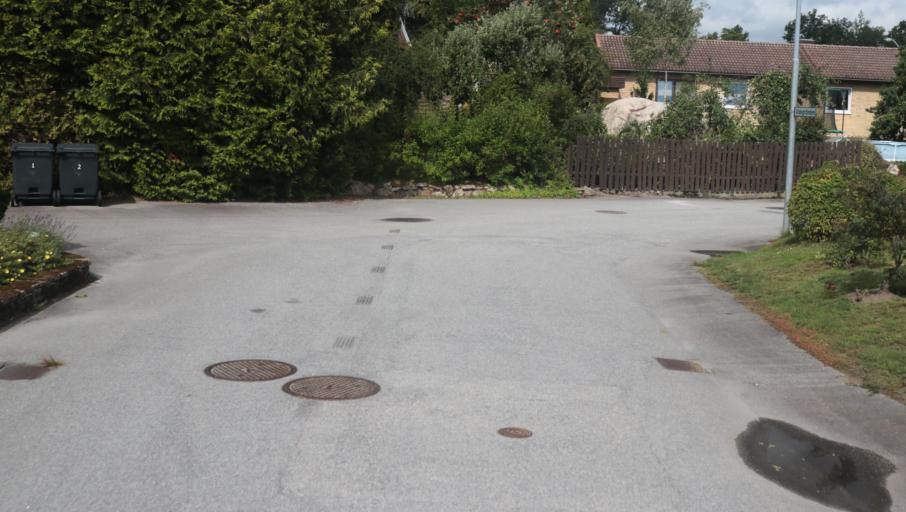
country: SE
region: Blekinge
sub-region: Karlshamns Kommun
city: Svangsta
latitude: 56.2611
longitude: 14.7637
